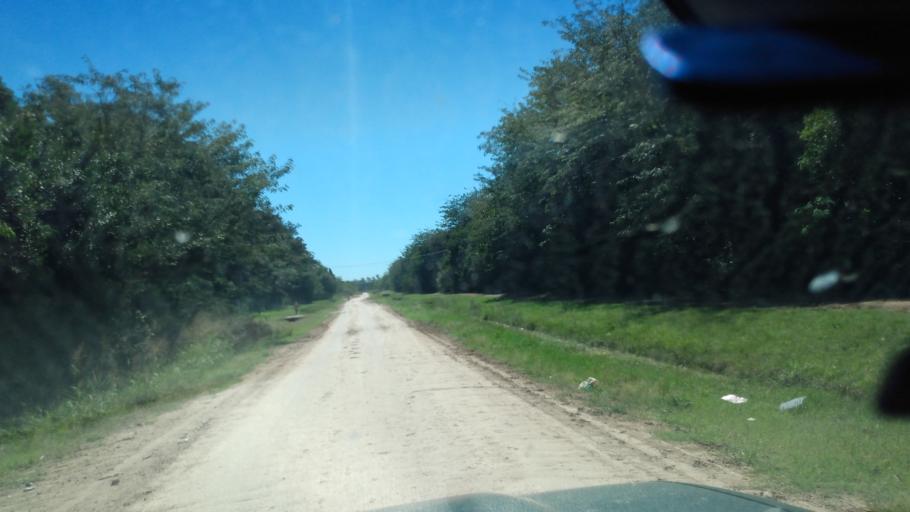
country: AR
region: Buenos Aires
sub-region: Partido de Lujan
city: Lujan
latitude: -34.5548
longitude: -59.1435
